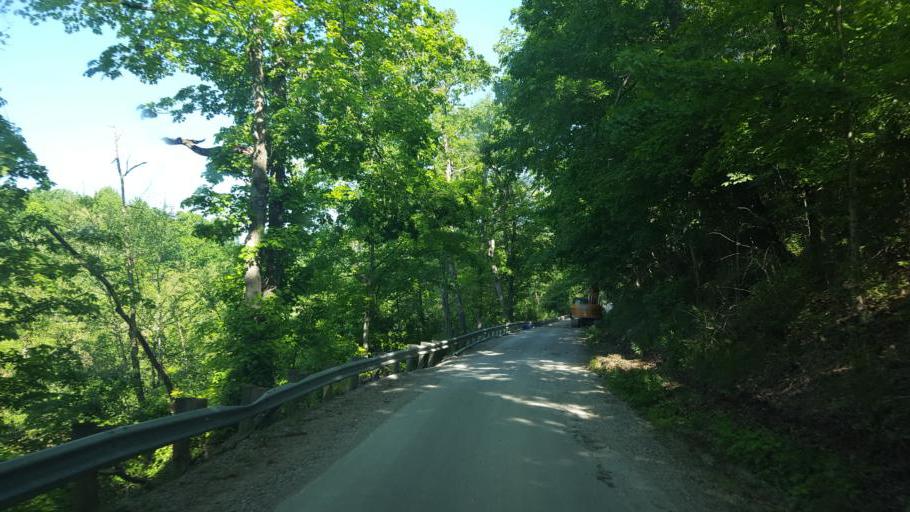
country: US
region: Ohio
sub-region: Jackson County
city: Wellston
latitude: 38.9931
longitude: -82.4105
